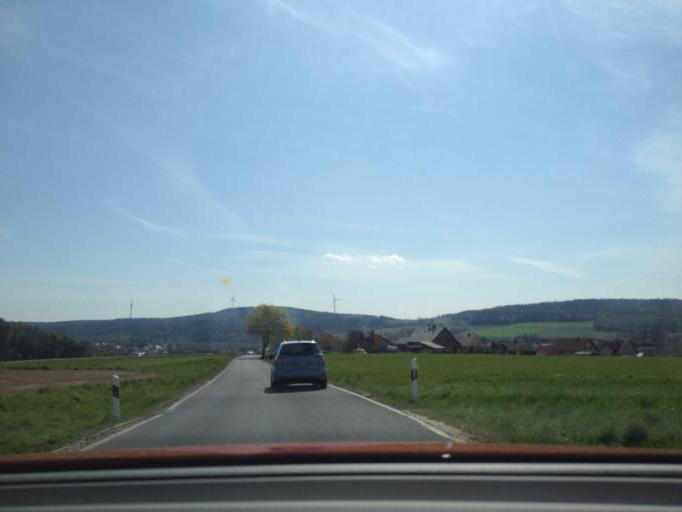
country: DE
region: Bavaria
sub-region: Upper Franconia
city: Arzberg
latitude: 50.0613
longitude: 12.1660
